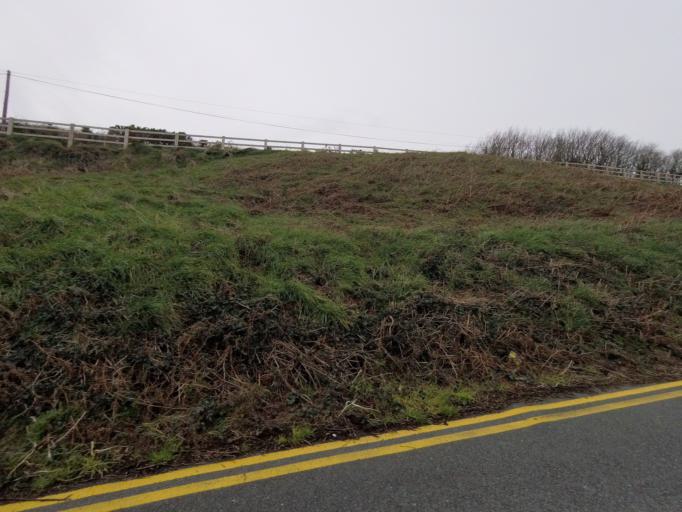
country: IE
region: Munster
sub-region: Waterford
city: Dunmore East
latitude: 52.1565
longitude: -6.9914
